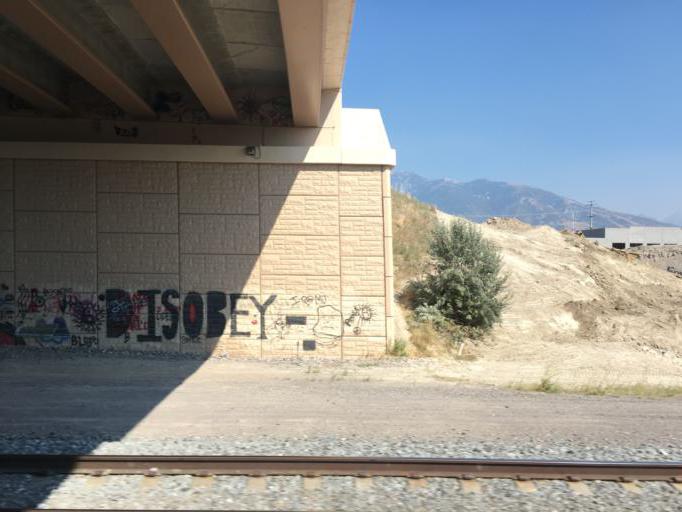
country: US
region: Utah
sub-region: Salt Lake County
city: South Jordan
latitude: 40.5443
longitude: -111.9029
